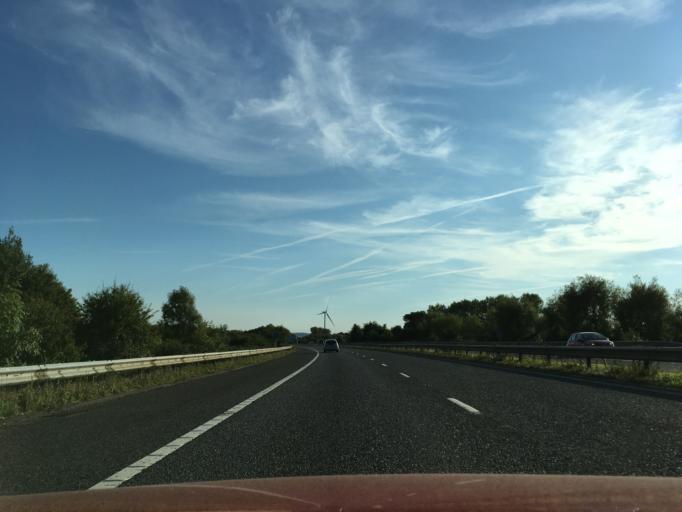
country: GB
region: England
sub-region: South Gloucestershire
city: Severn Beach
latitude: 51.5241
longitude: -2.6572
